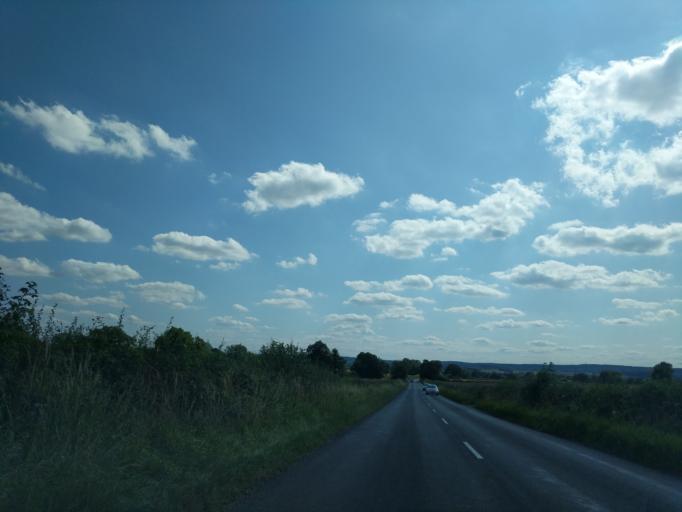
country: GB
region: England
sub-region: Staffordshire
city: Rugeley
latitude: 52.7998
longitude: -1.9305
